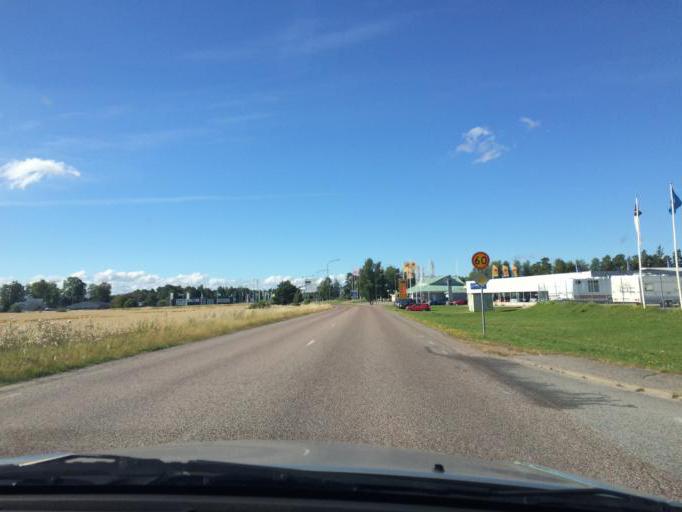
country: SE
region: Vaestmanland
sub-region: Vasteras
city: Hokasen
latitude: 59.6143
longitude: 16.6162
